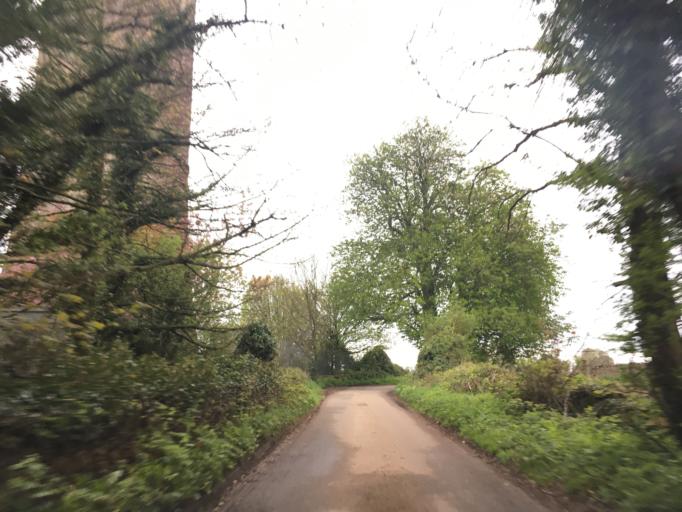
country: GB
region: England
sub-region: Gloucestershire
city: Wotton-under-Edge
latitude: 51.6498
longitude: -2.3039
